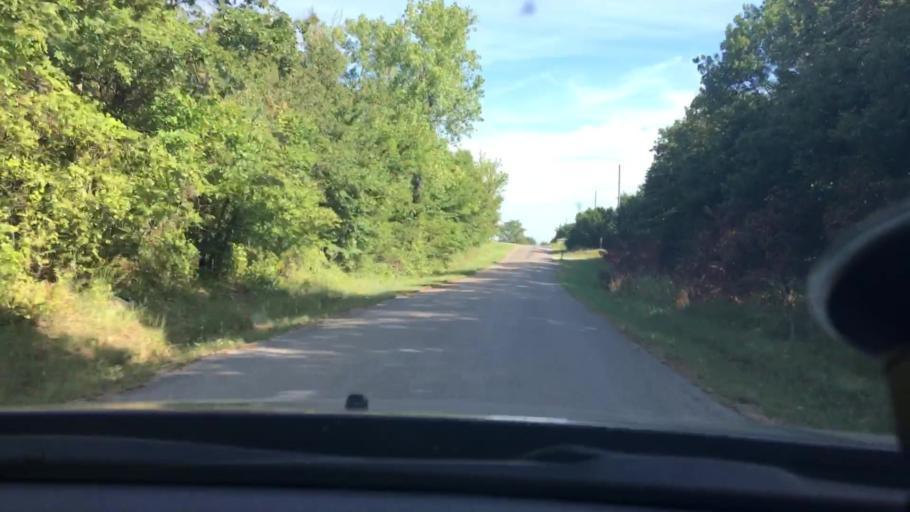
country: US
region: Oklahoma
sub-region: Carter County
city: Lone Grove
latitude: 34.2553
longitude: -97.2474
